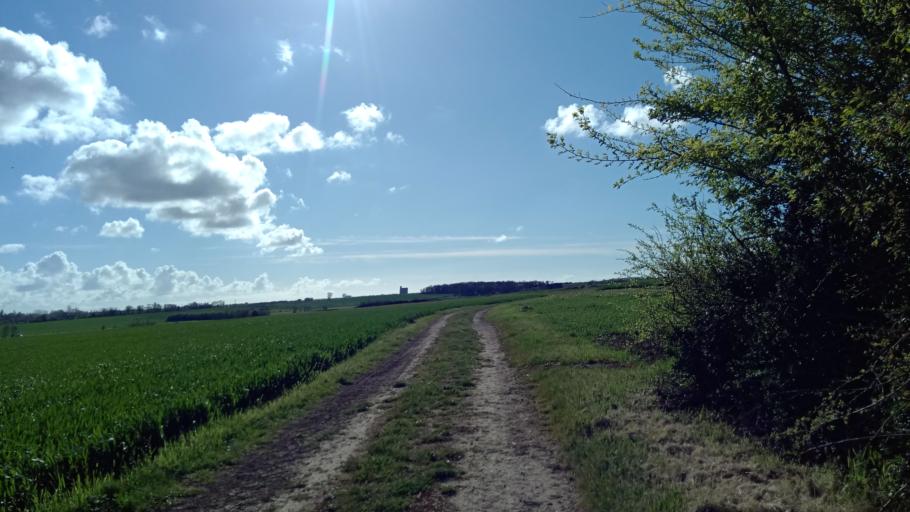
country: FR
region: Poitou-Charentes
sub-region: Departement de la Charente-Maritime
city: Verines
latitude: 46.1572
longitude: -0.9368
